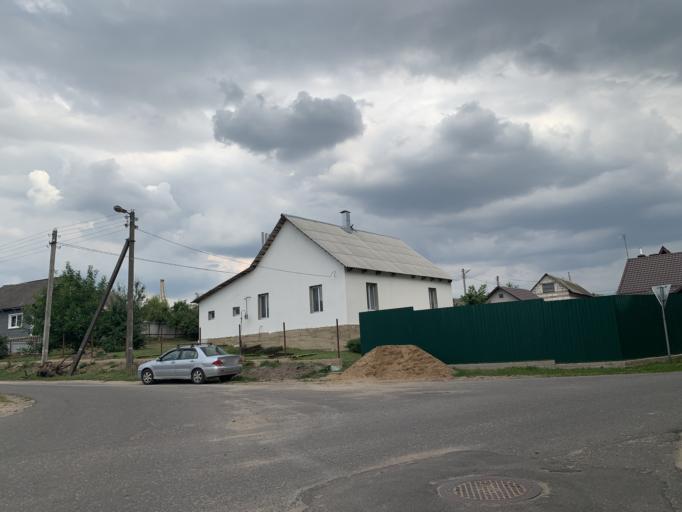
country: BY
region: Minsk
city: Nyasvizh
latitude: 53.2110
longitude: 26.6929
